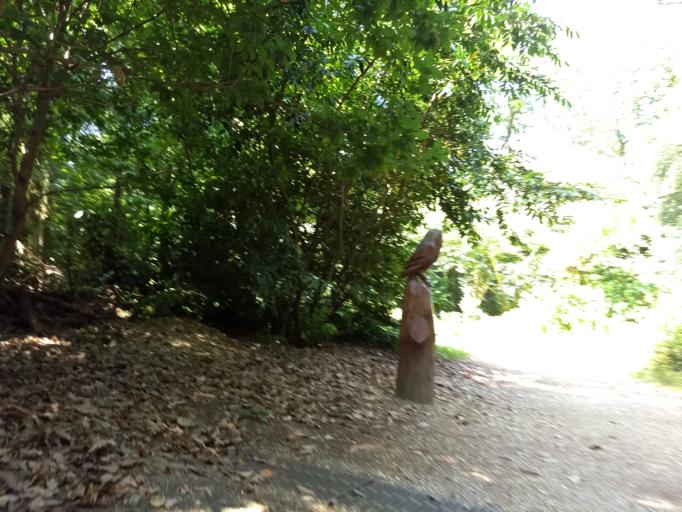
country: GB
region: England
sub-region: Isle of Wight
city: East Cowes
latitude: 50.7531
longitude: -1.2553
